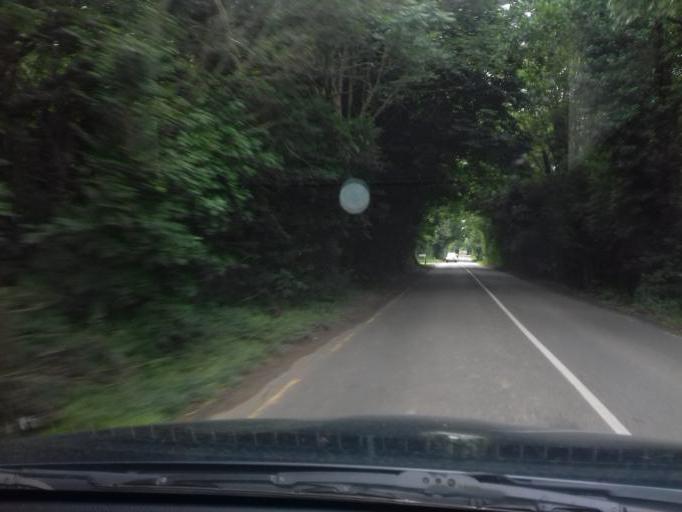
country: IE
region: Leinster
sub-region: Loch Garman
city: Castlebridge
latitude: 52.4423
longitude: -6.4018
